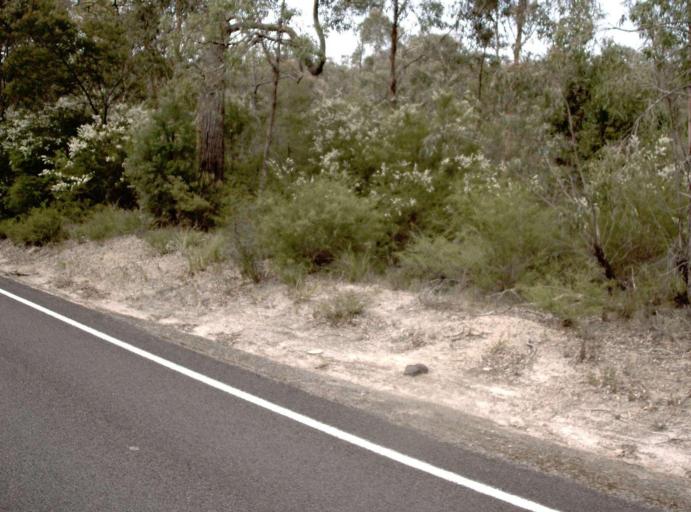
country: AU
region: New South Wales
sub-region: Bega Valley
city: Eden
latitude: -37.4882
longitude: 149.5503
